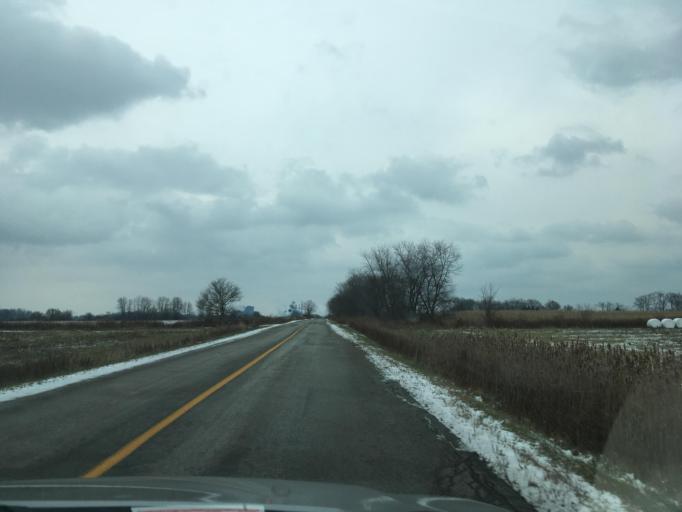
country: CA
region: Ontario
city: Norfolk County
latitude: 42.7898
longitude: -80.1326
